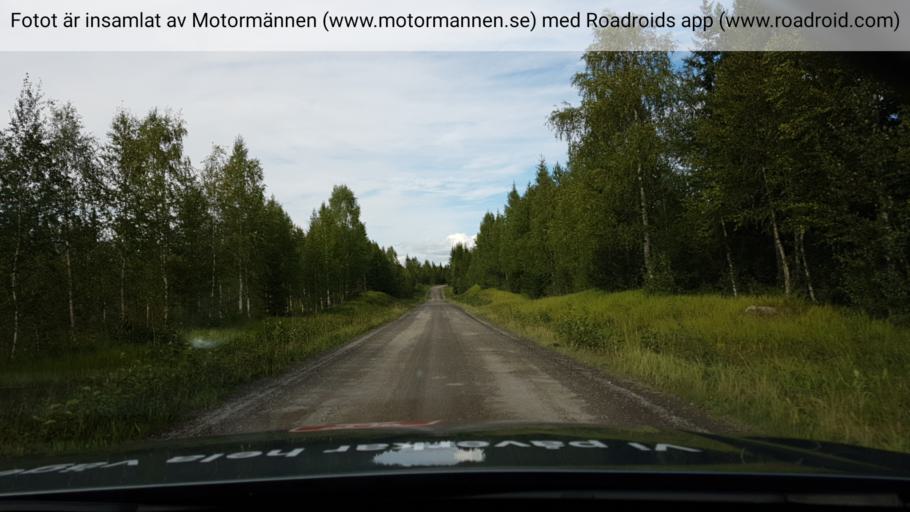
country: SE
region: Jaemtland
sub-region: Braecke Kommun
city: Braecke
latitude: 63.2352
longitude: 15.3608
